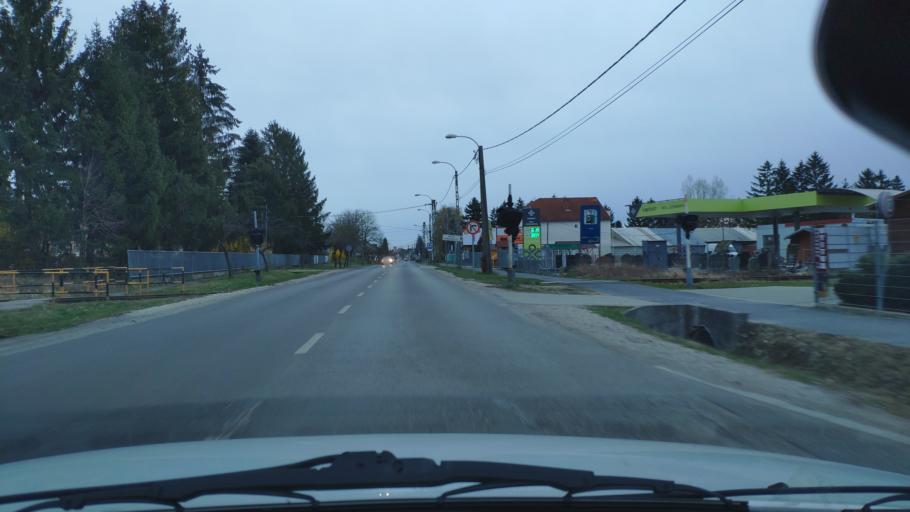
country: HU
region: Zala
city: Nagykanizsa
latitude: 46.4723
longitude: 16.9857
